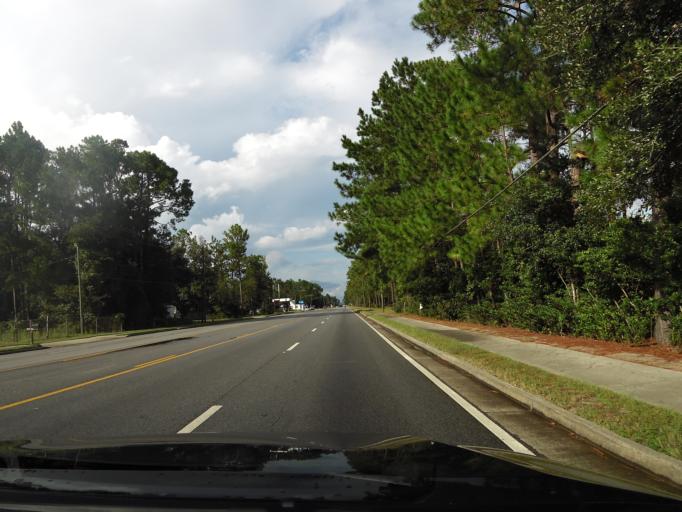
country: US
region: Georgia
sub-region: Liberty County
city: Walthourville
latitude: 31.8015
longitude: -81.6053
